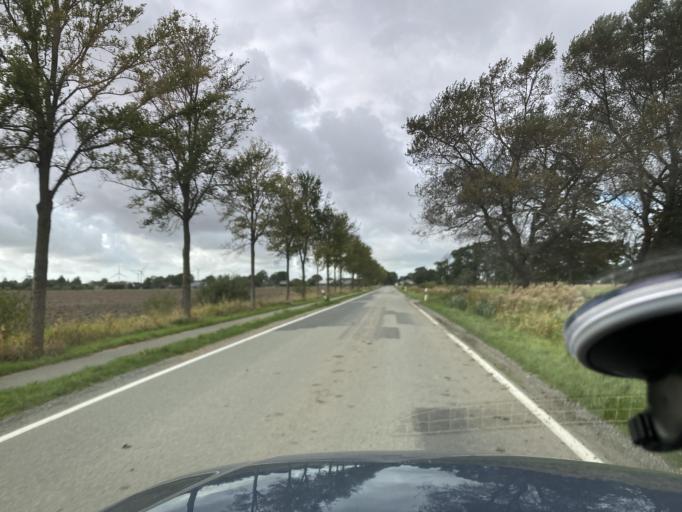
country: DE
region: Schleswig-Holstein
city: Neuenkirchen
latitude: 54.2344
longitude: 9.0080
